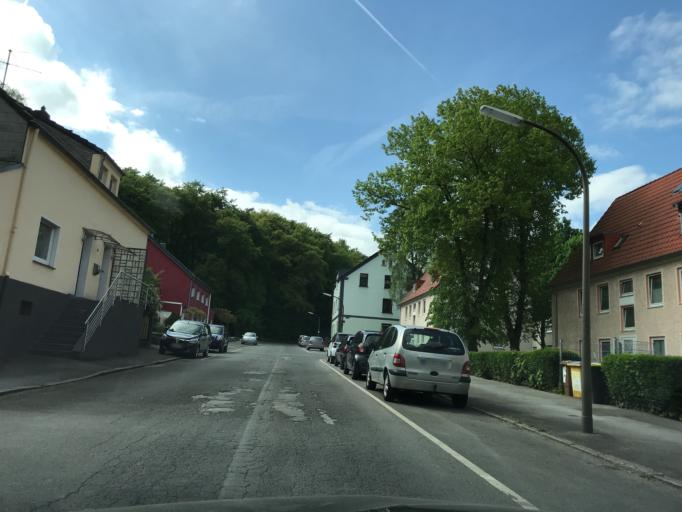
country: DE
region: North Rhine-Westphalia
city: Witten
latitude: 51.4854
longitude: 7.3693
